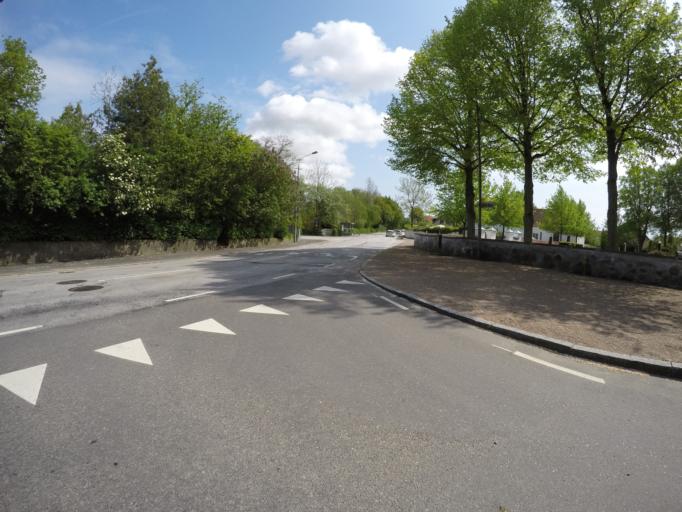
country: SE
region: Skane
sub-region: Malmo
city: Tygelsjo
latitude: 55.5284
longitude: 12.9952
